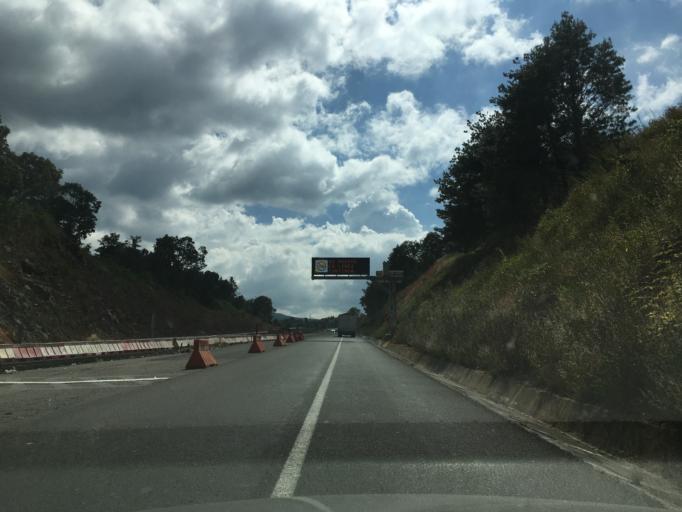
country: MX
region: Michoacan
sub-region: Patzcuaro
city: Colonia Vista Bella (Lomas del Peaje)
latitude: 19.5189
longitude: -101.5734
